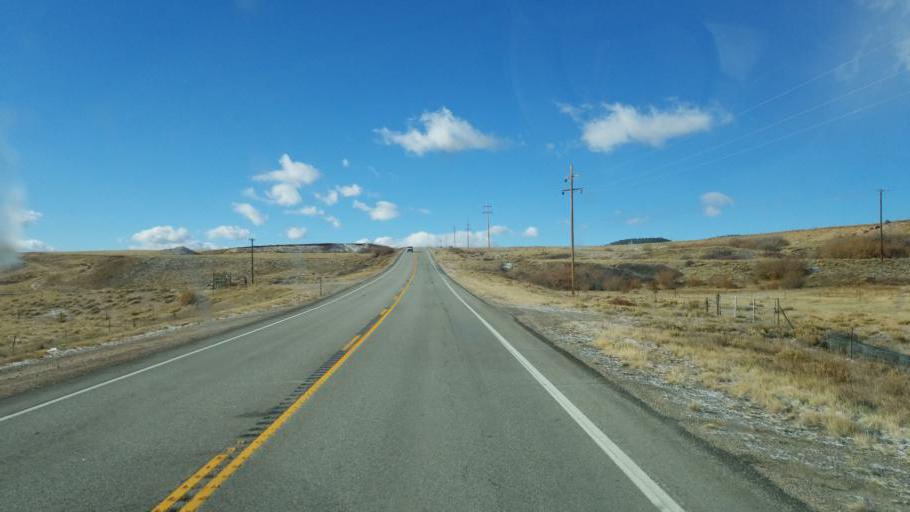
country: US
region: Colorado
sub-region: Park County
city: Fairplay
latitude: 39.3323
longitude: -105.8675
